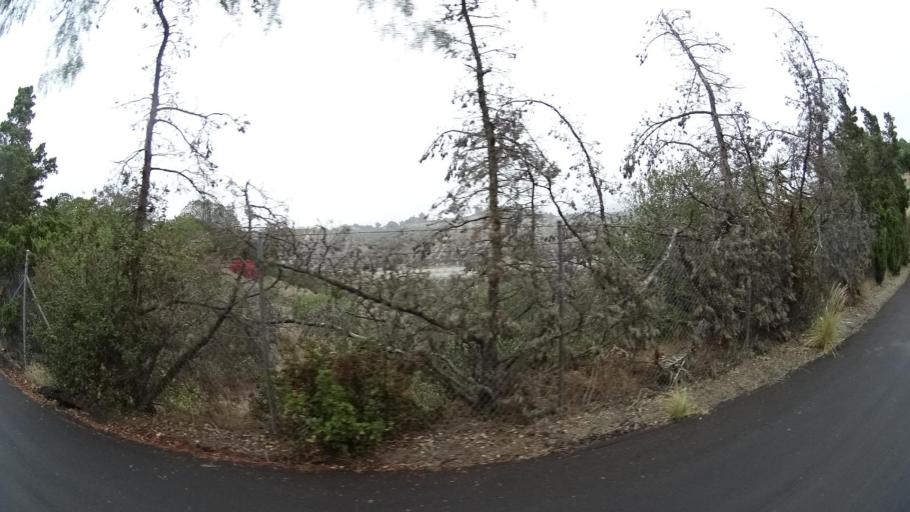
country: US
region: California
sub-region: San Diego County
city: Rainbow
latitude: 33.3816
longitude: -117.1769
